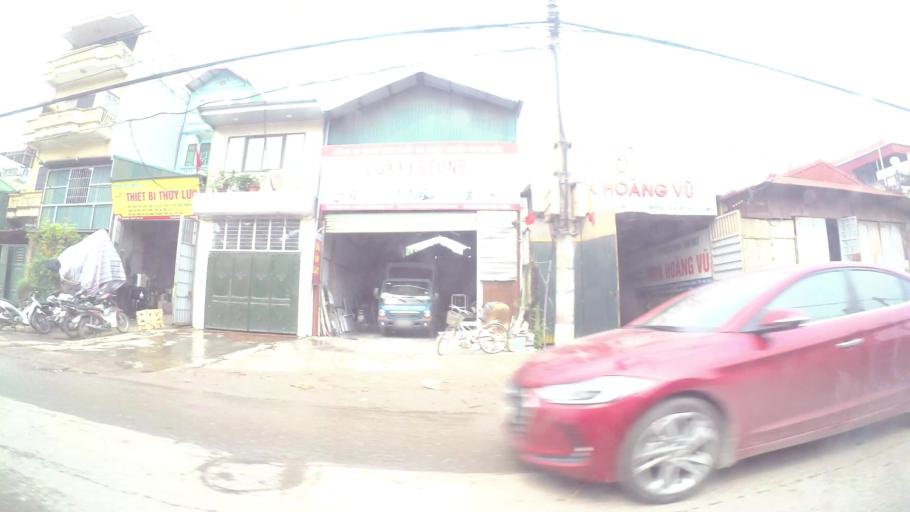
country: VN
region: Ha Noi
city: Van Dien
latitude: 20.9723
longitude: 105.8665
